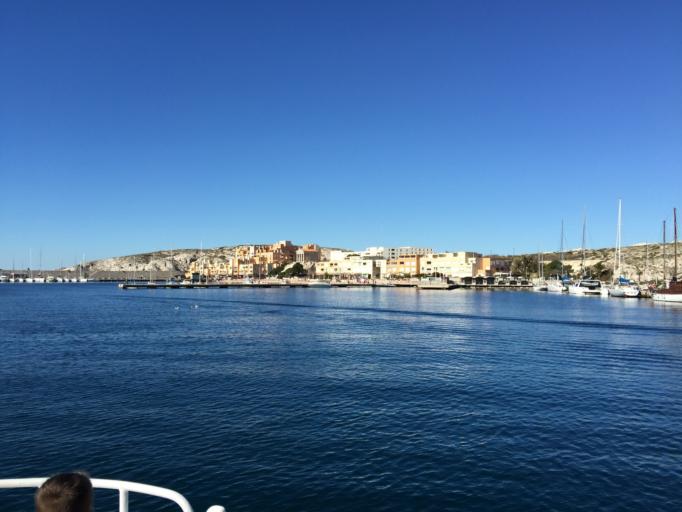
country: FR
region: Provence-Alpes-Cote d'Azur
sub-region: Departement des Bouches-du-Rhone
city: Marseille 07
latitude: 43.2779
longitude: 5.3084
